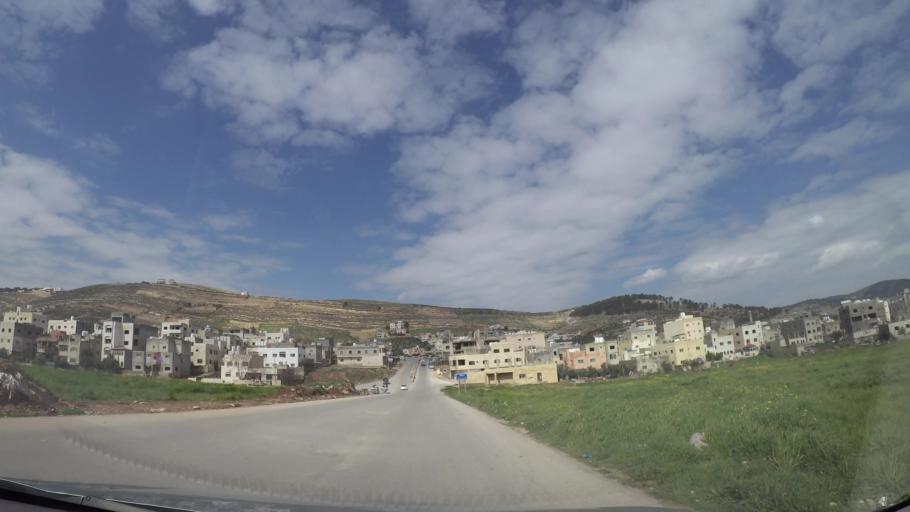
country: JO
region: Amman
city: Al Jubayhah
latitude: 32.0669
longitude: 35.8178
